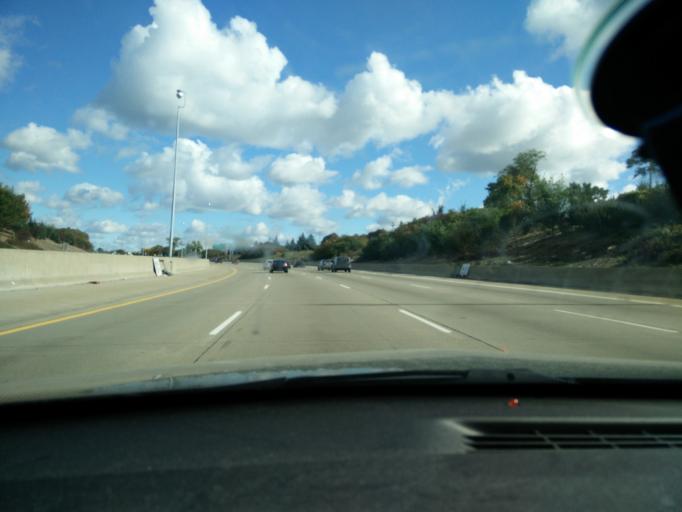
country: US
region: Michigan
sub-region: Oakland County
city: Madison Heights
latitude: 42.4779
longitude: -83.0902
